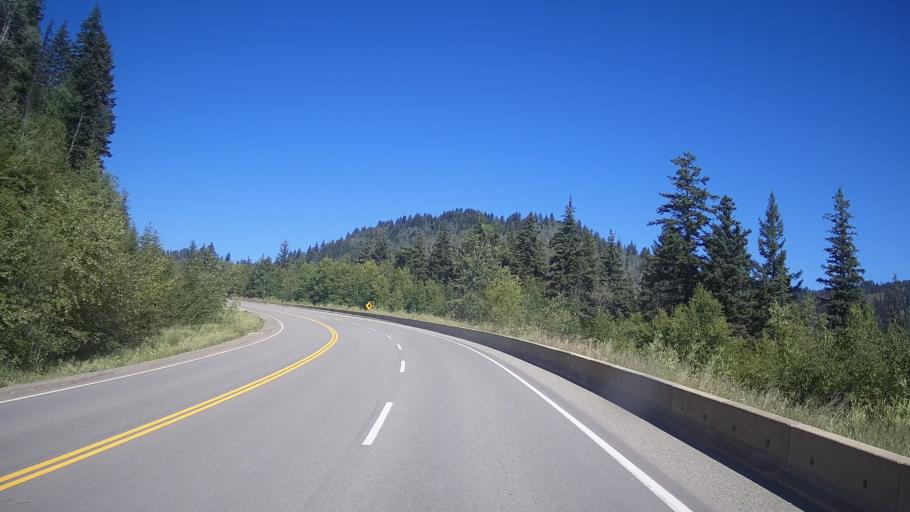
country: CA
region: British Columbia
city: Kamloops
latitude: 51.4944
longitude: -120.2722
